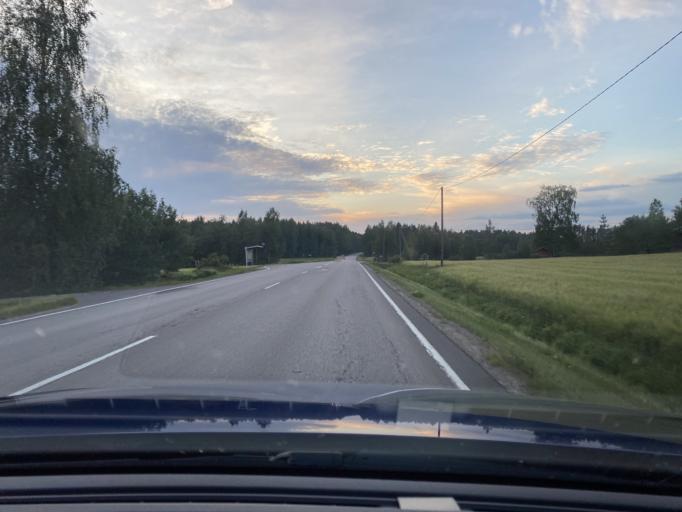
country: FI
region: Satakunta
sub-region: Pohjois-Satakunta
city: Honkajoki
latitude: 61.9042
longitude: 22.2729
